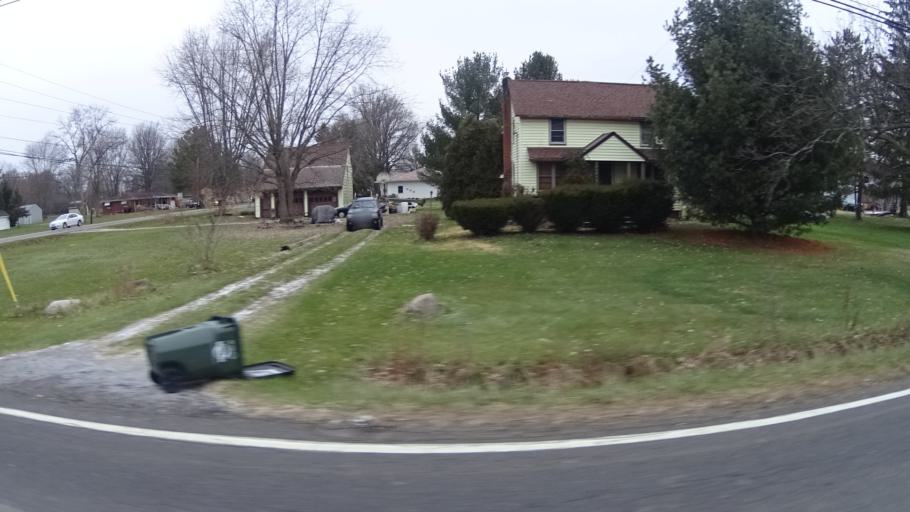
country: US
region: Ohio
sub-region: Lorain County
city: Grafton
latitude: 41.3027
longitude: -82.0510
